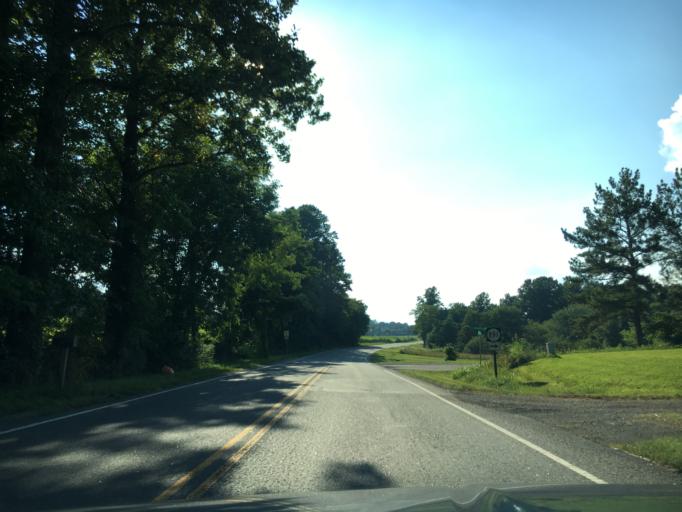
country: US
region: Virginia
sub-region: City of Bedford
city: Bedford
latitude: 37.2254
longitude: -79.5204
